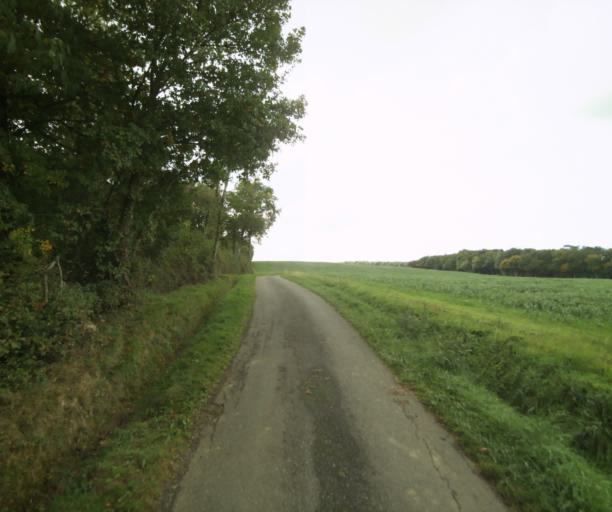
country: FR
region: Midi-Pyrenees
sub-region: Departement du Gers
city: Gondrin
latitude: 43.8617
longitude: 0.2222
